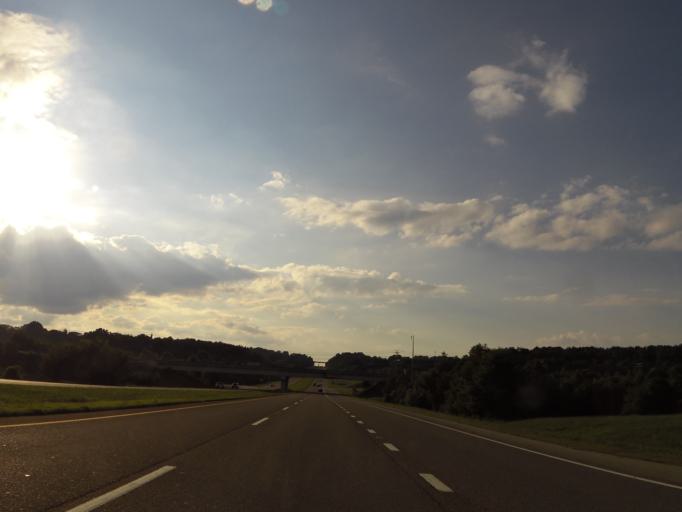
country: US
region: Tennessee
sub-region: Knox County
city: Farragut
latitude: 35.9240
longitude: -84.1319
